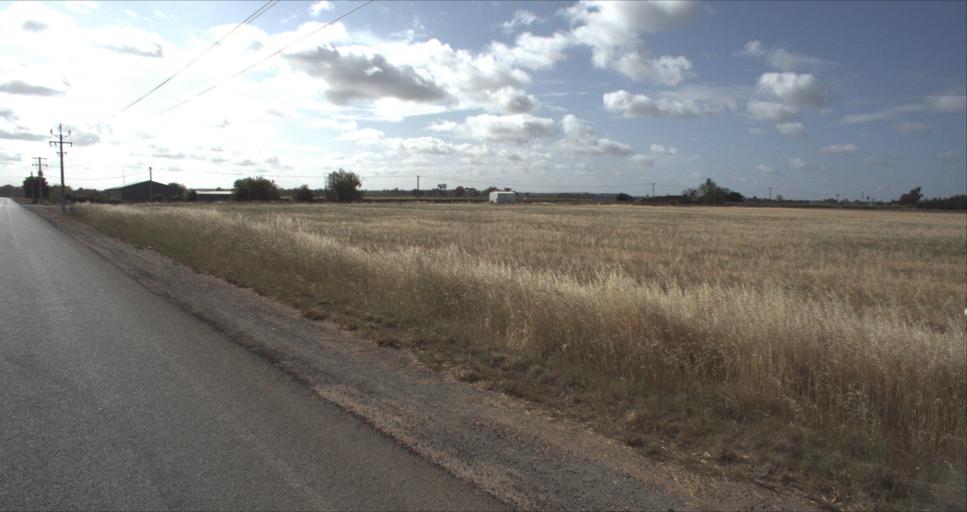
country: AU
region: New South Wales
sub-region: Leeton
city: Leeton
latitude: -34.5714
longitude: 146.3975
